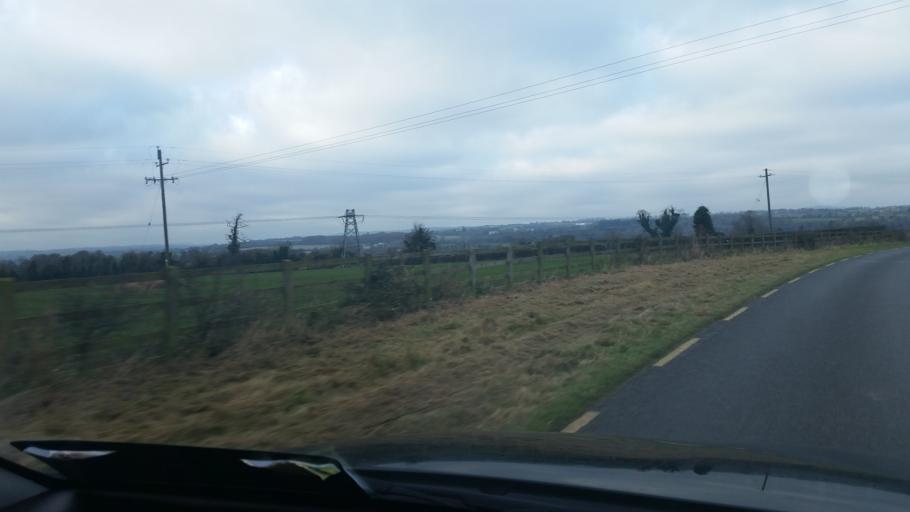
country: IE
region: Leinster
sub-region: Lu
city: Tullyallen
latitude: 53.7110
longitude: -6.4135
